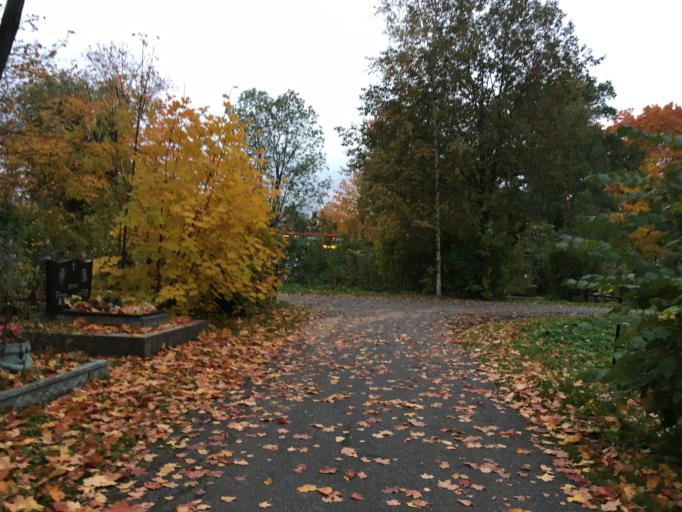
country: RU
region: St.-Petersburg
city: Centralniy
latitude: 59.9015
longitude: 30.3725
